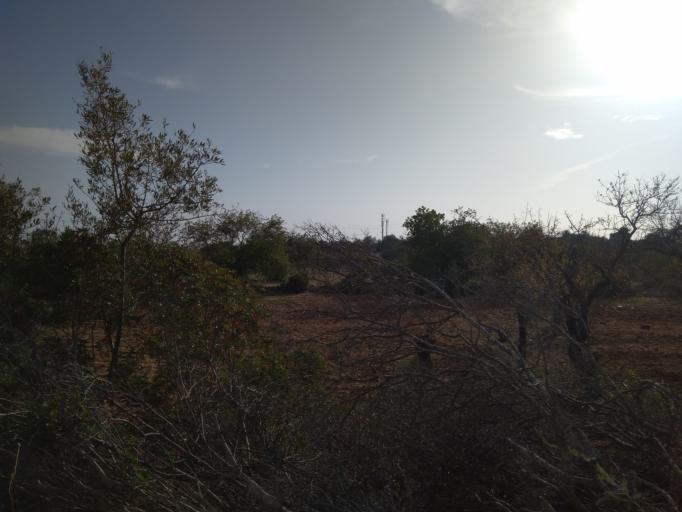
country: PT
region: Faro
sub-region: Faro
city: Santa Barbara de Nexe
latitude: 37.0991
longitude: -7.9595
